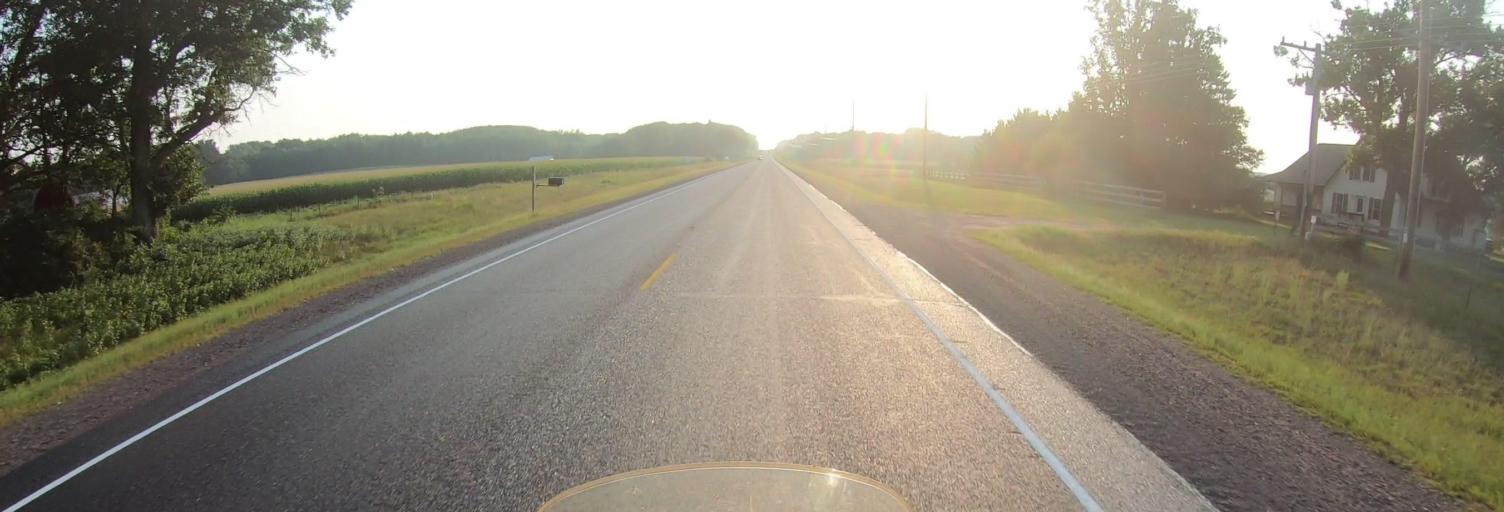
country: US
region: Wisconsin
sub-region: Washburn County
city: Shell Lake
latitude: 45.8153
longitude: -92.0117
